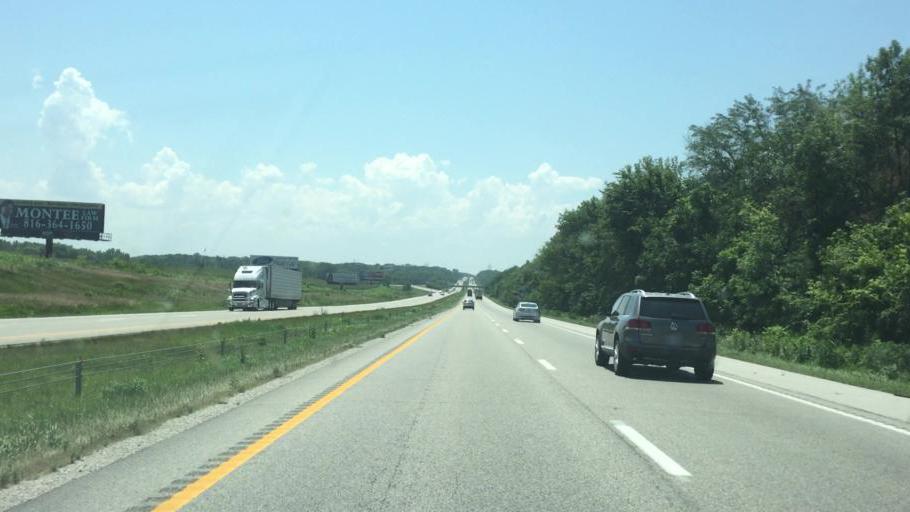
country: US
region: Missouri
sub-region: Platte County
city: Platte City
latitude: 39.5256
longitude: -94.7872
